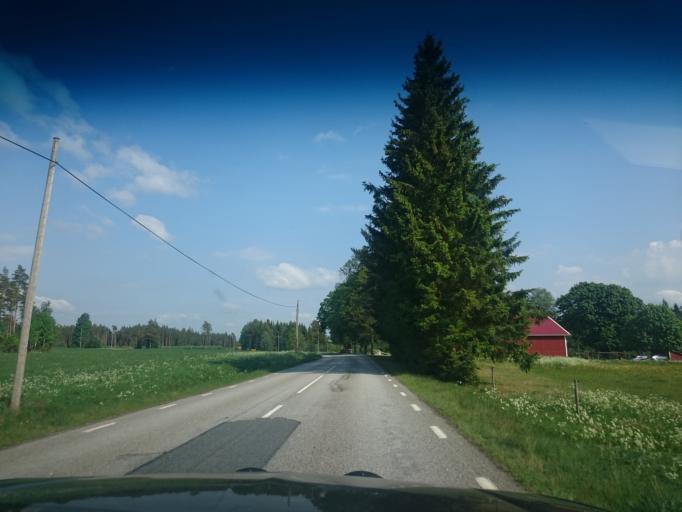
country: SE
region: Joenkoeping
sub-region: Vetlanda Kommun
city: Landsbro
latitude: 57.3799
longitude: 14.9876
